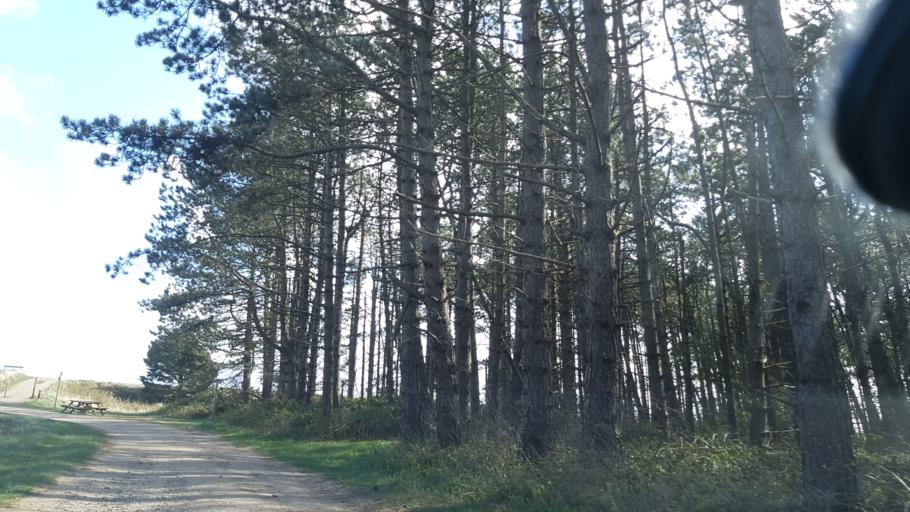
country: DE
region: Schleswig-Holstein
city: List
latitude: 55.0829
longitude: 8.5313
